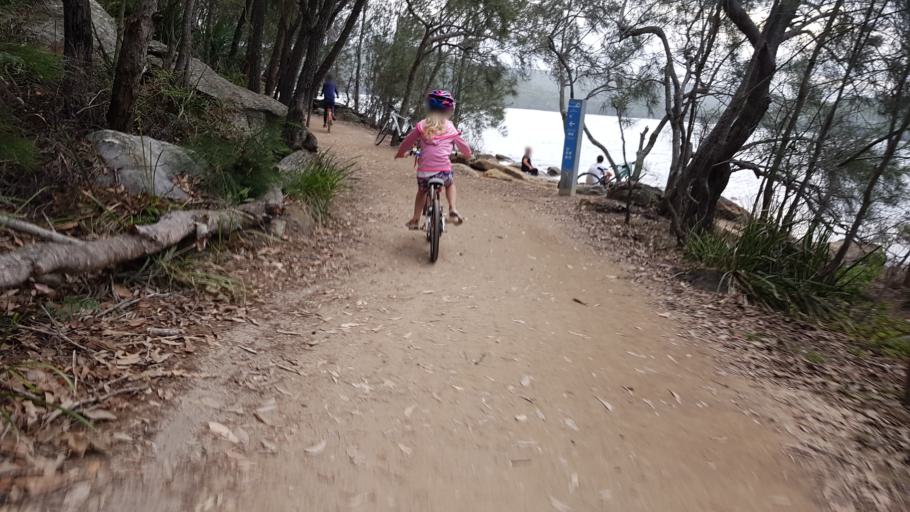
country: AU
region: New South Wales
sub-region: Pittwater
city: North Narrabeen
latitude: -33.7144
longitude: 151.2814
